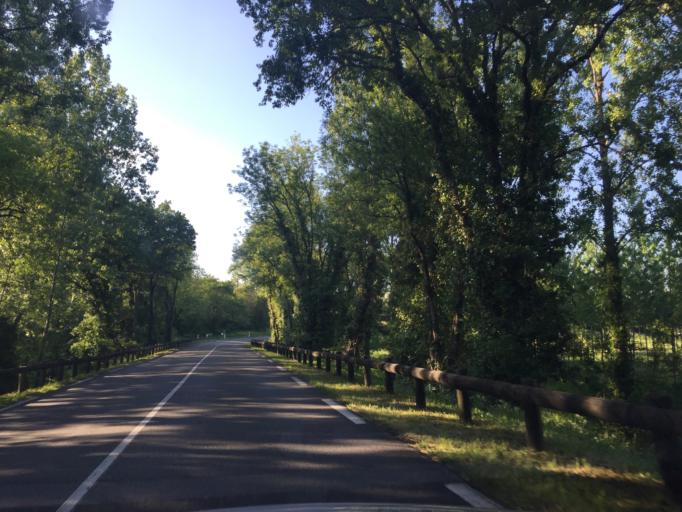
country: FR
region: Aquitaine
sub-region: Departement de la Dordogne
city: La Roche-Chalais
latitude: 45.2091
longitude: 0.0326
